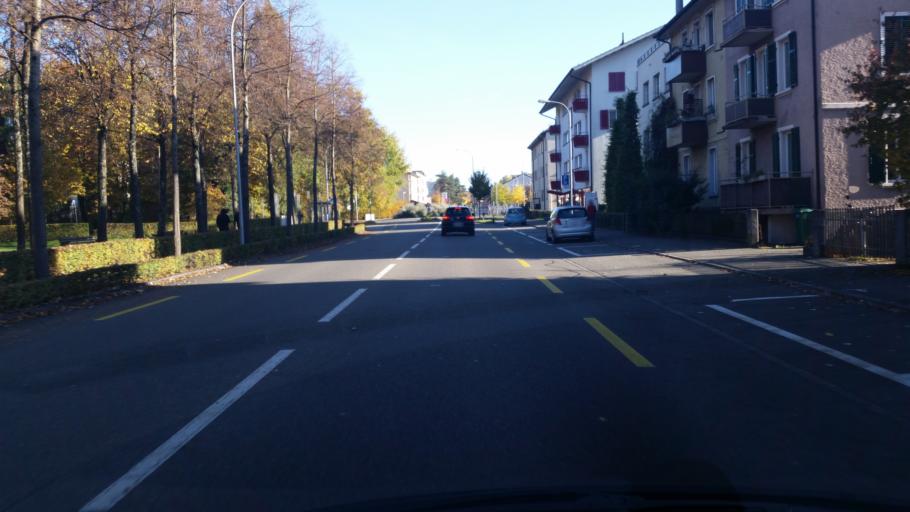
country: CH
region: Aargau
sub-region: Bezirk Baden
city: Neuenhof
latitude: 47.4634
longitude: 8.3257
